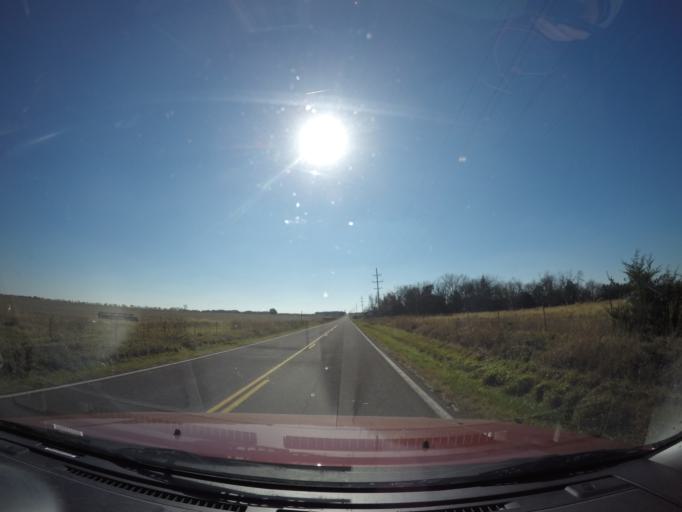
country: US
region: Kansas
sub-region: Morris County
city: Council Grove
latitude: 38.8676
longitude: -96.5939
